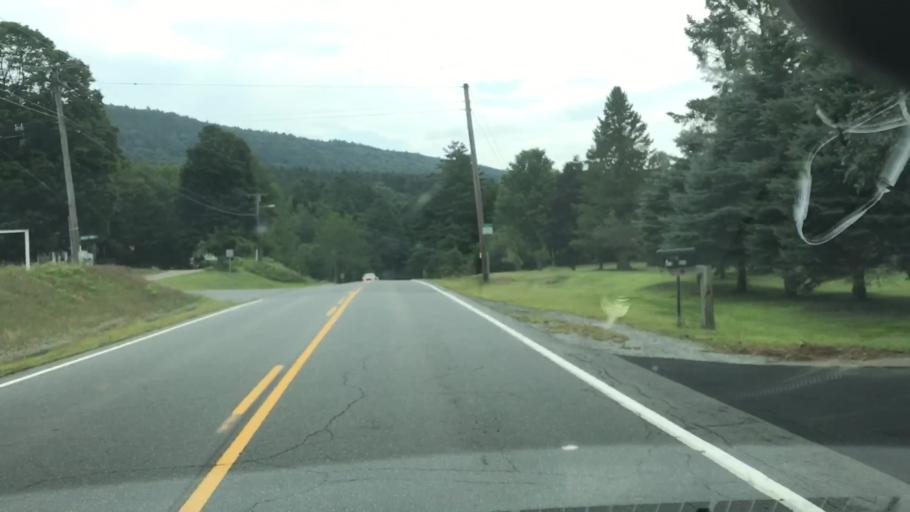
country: US
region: New Hampshire
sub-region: Grafton County
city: Woodsville
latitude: 44.2442
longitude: -72.0436
